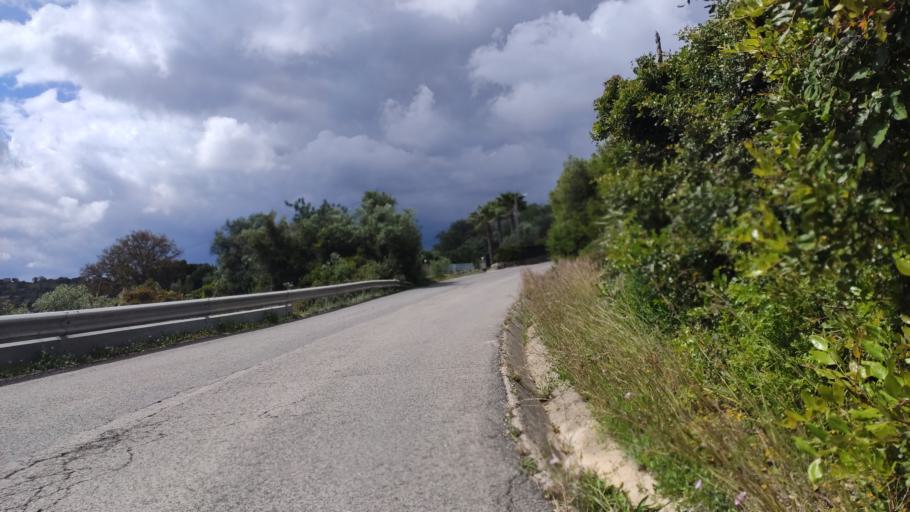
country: PT
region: Faro
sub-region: Sao Bras de Alportel
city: Sao Bras de Alportel
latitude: 37.1579
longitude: -7.9395
